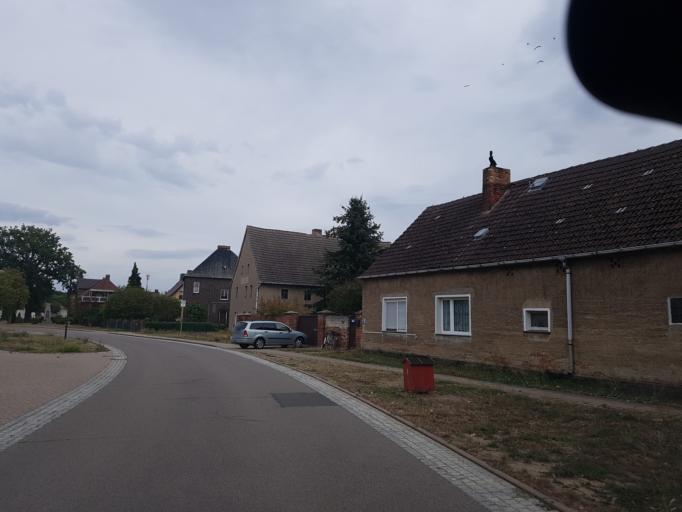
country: DE
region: Saxony-Anhalt
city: Annaburg
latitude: 51.7815
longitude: 13.0487
